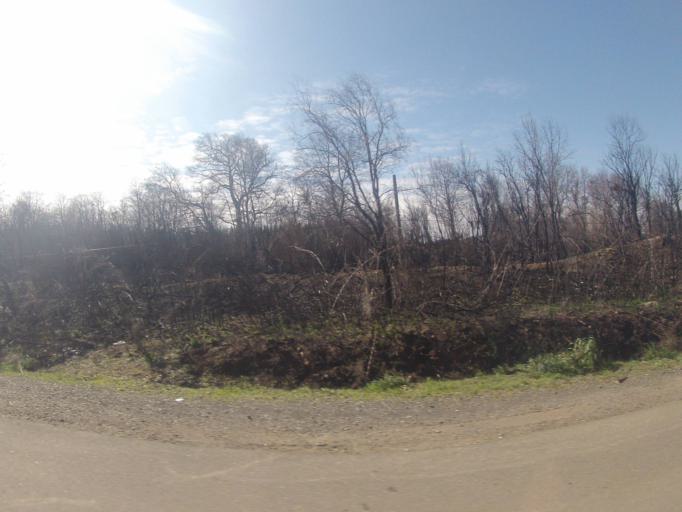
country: CL
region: Araucania
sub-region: Provincia de Malleco
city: Victoria
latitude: -38.1520
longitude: -72.3064
